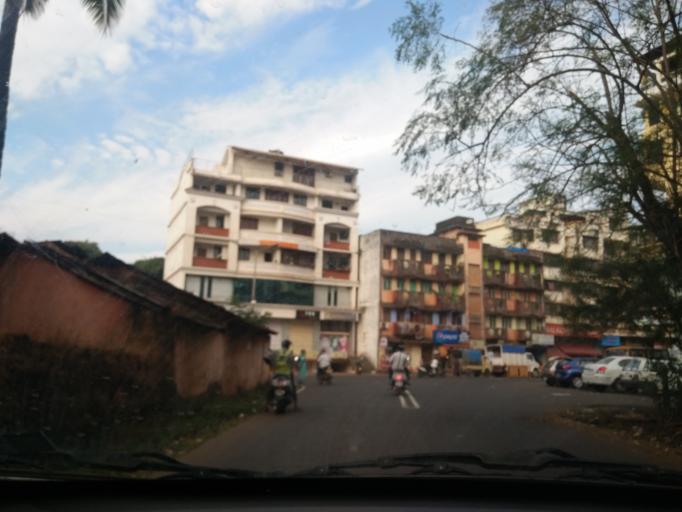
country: IN
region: Goa
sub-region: South Goa
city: Davorlim
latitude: 15.2824
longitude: 73.9789
